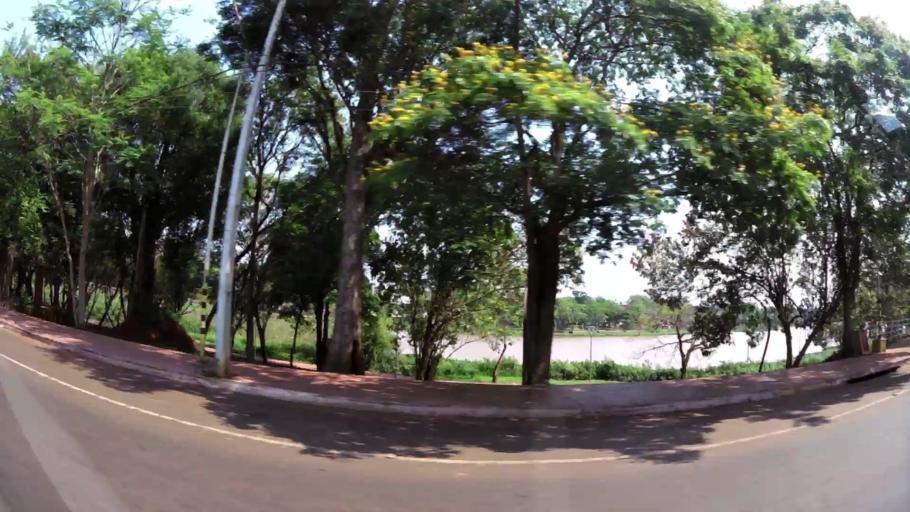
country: PY
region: Alto Parana
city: Presidente Franco
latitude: -25.5202
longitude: -54.6225
